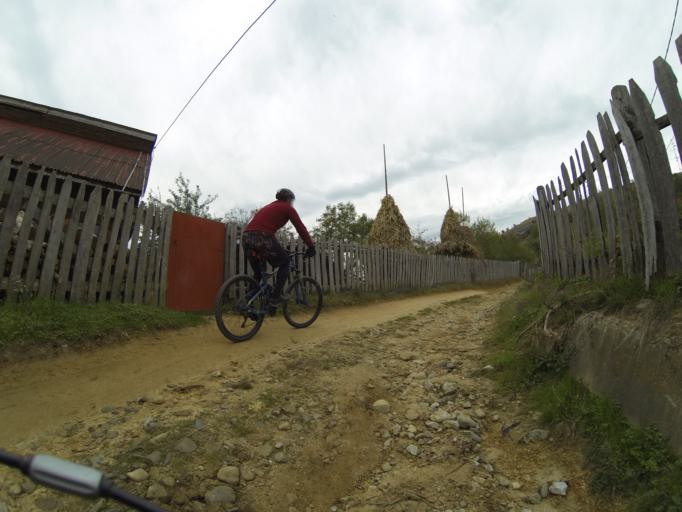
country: RO
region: Gorj
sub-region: Comuna Tismana
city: Sohodol
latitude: 45.0589
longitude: 22.8858
